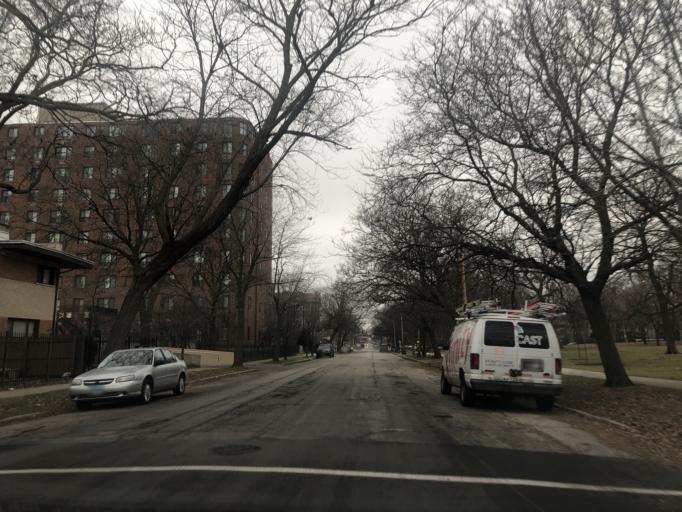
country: US
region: Illinois
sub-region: Cook County
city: Chicago
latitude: 41.7858
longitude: -87.6132
